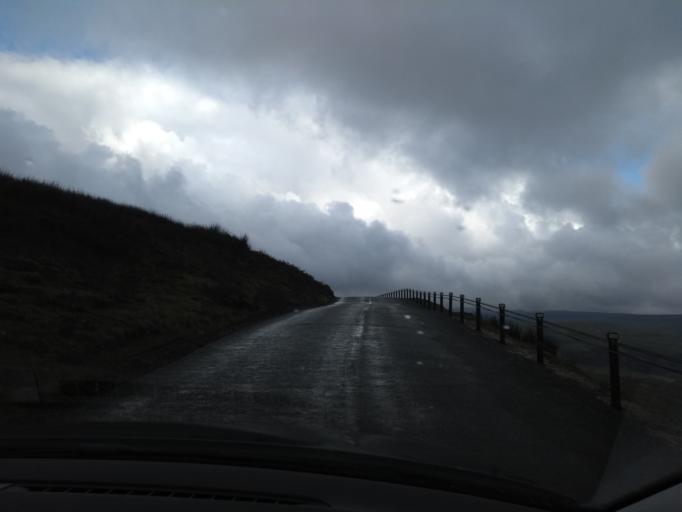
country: GB
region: England
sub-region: Cumbria
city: Kirkby Stephen
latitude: 54.3656
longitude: -2.1896
